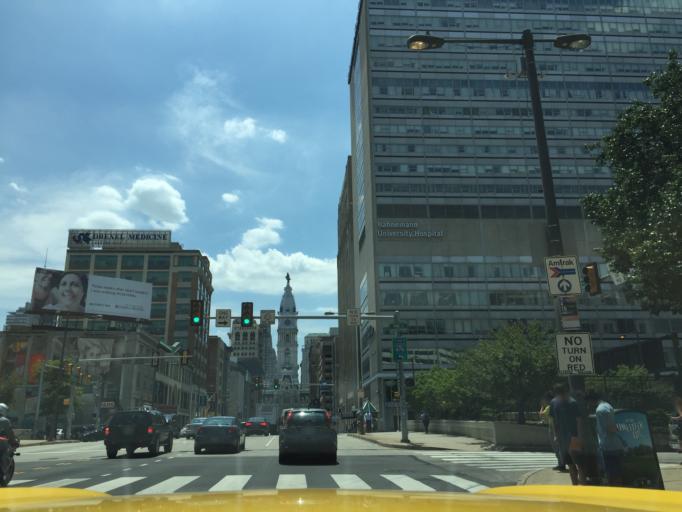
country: US
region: Pennsylvania
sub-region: Philadelphia County
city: Philadelphia
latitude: 39.9583
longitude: -75.1624
